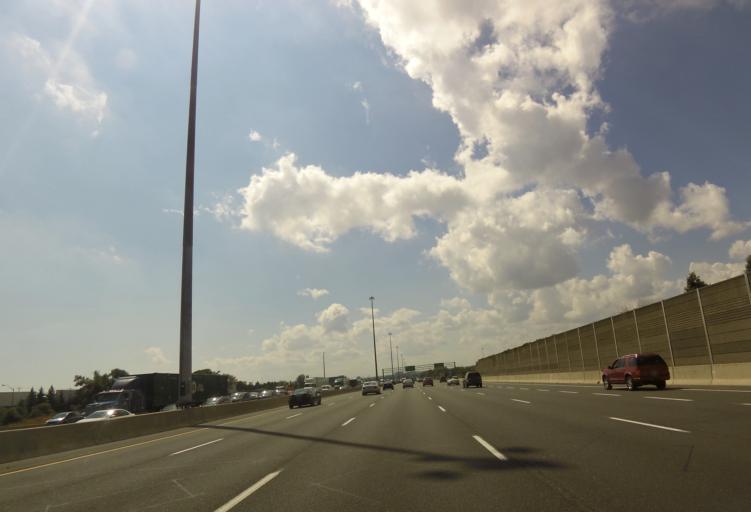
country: CA
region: Ontario
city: Ajax
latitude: 43.8509
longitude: -79.0319
